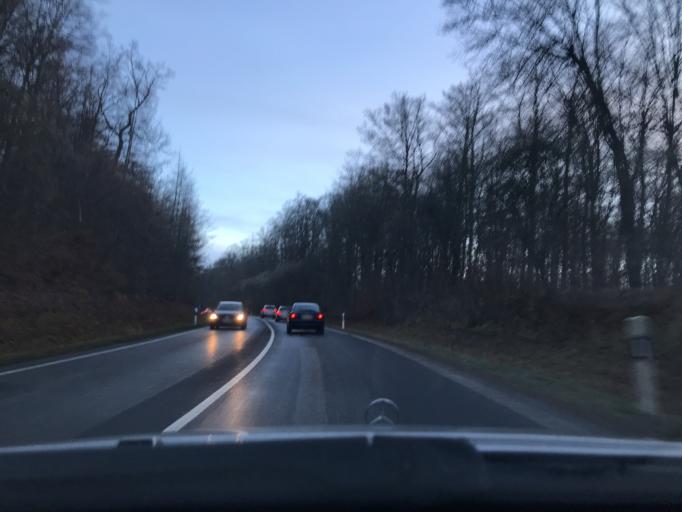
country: DE
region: Hesse
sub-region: Regierungsbezirk Kassel
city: Calden
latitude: 51.3962
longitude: 9.4293
